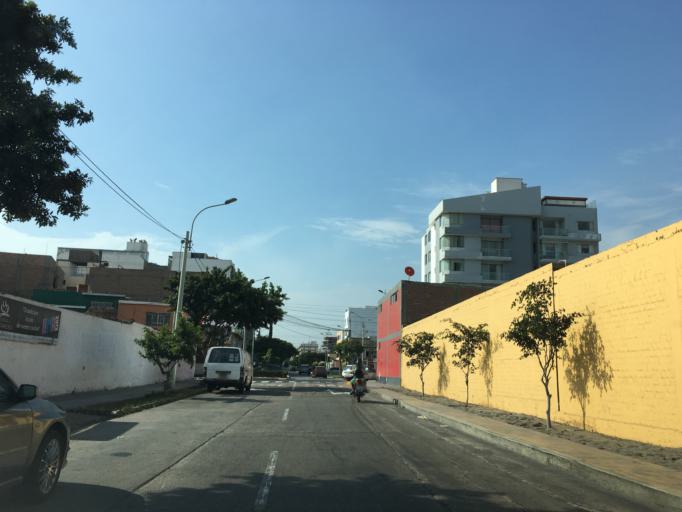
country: PE
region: Lima
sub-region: Lima
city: San Isidro
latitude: -12.0760
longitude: -77.0624
